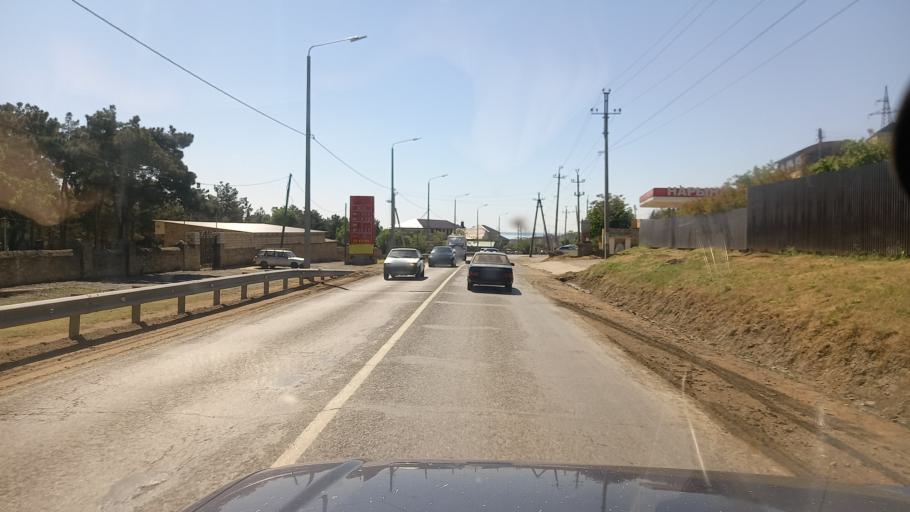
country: RU
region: Dagestan
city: Derbent
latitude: 42.0465
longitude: 48.2853
